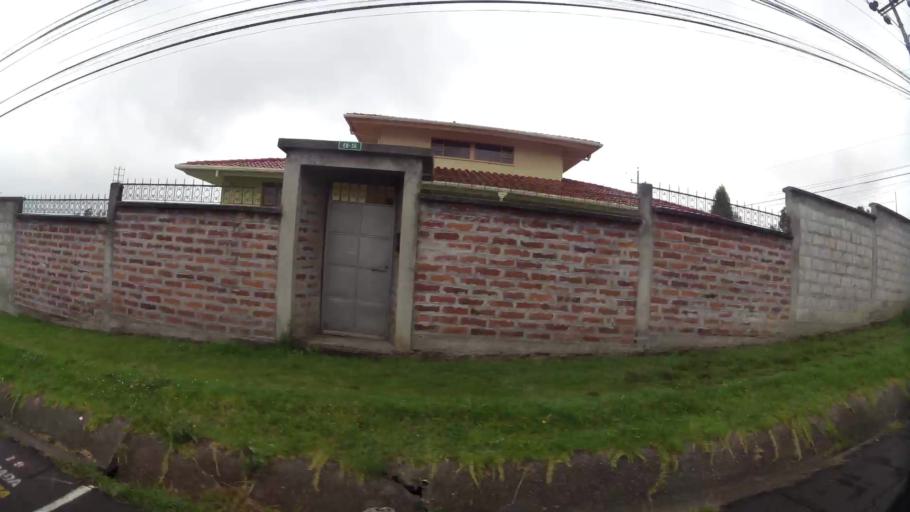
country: EC
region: Pichincha
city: Sangolqui
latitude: -0.2800
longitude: -78.4610
